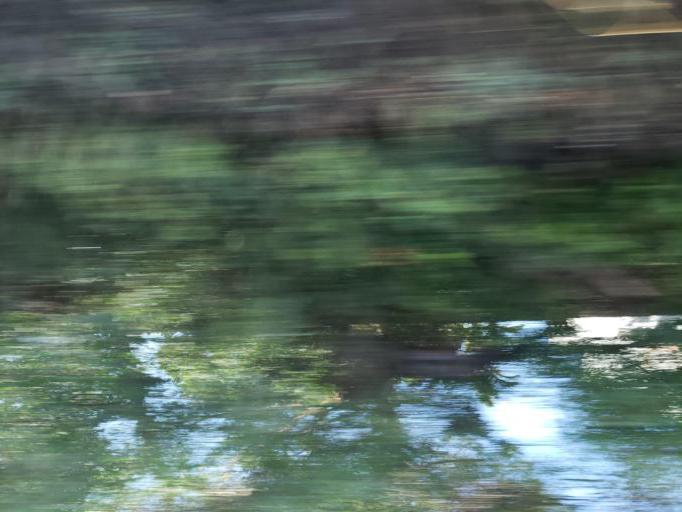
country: PT
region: Faro
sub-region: Portimao
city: Alvor
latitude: 37.1849
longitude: -8.5860
